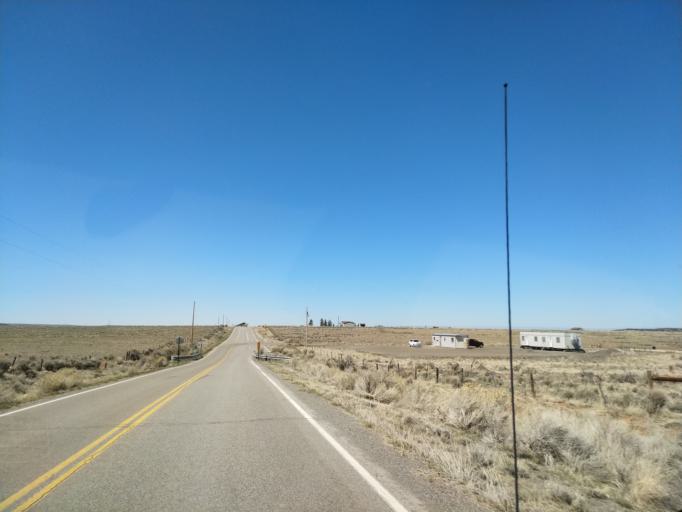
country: US
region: Colorado
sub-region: Mesa County
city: Redlands
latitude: 38.9938
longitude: -108.7442
